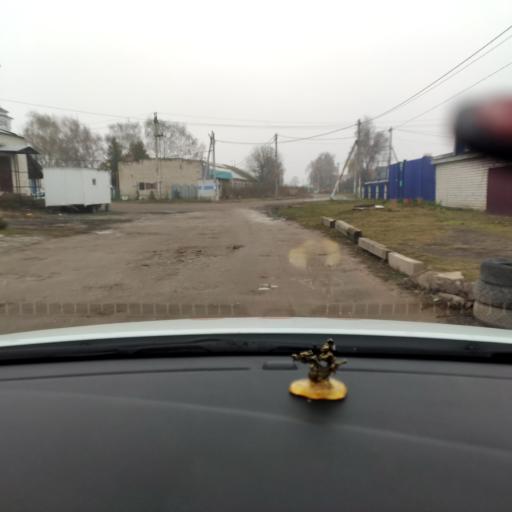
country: RU
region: Tatarstan
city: Osinovo
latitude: 55.8818
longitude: 48.8817
